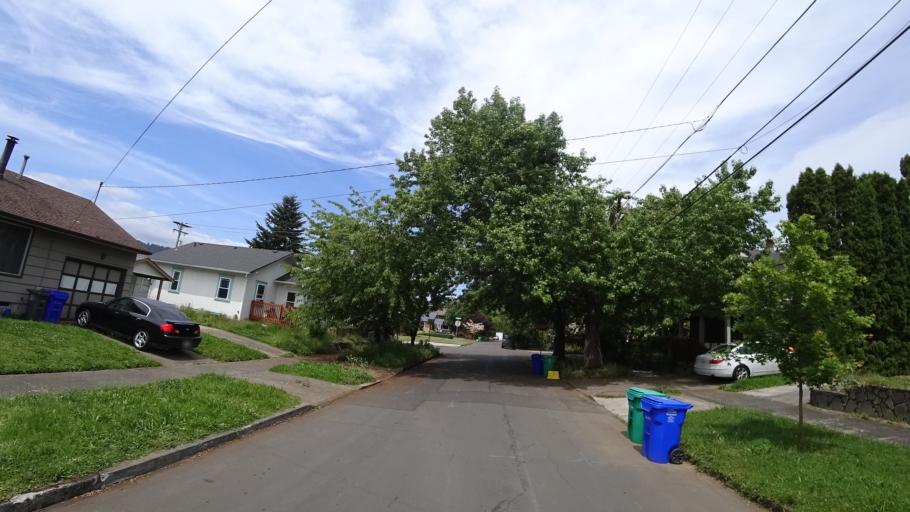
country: US
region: Oregon
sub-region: Washington County
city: West Haven
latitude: 45.5950
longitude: -122.7632
